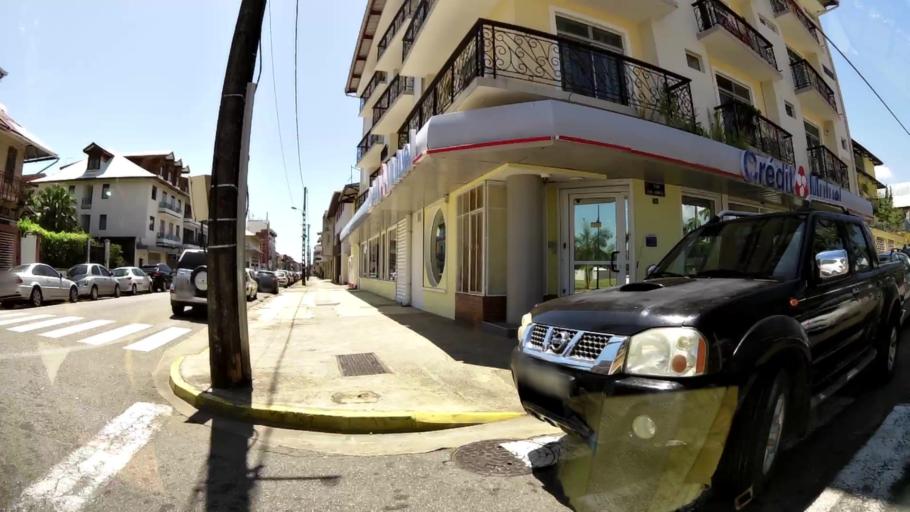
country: GF
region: Guyane
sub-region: Guyane
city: Cayenne
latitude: 4.9397
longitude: -52.3333
